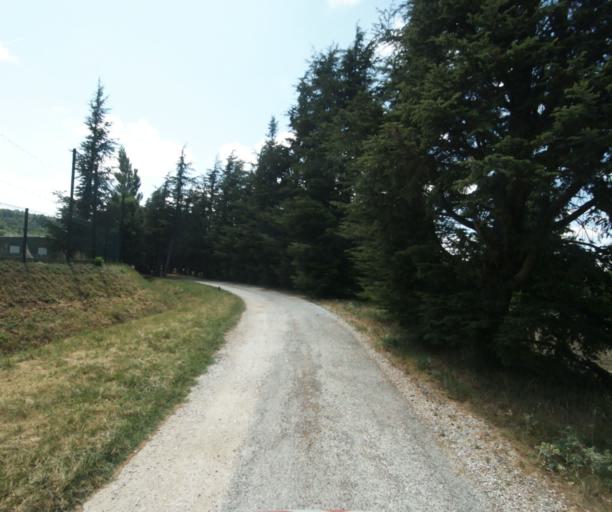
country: FR
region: Midi-Pyrenees
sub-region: Departement de la Haute-Garonne
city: Revel
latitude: 43.4536
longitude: 2.0134
